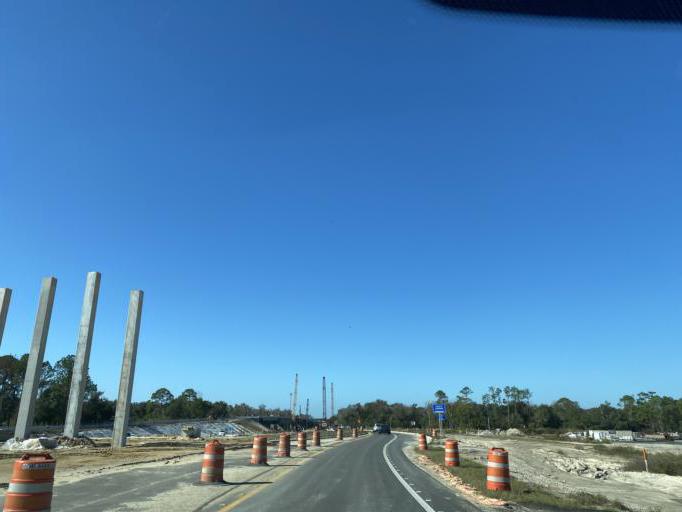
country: US
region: Florida
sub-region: Seminole County
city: Heathrow
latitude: 28.8153
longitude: -81.4132
